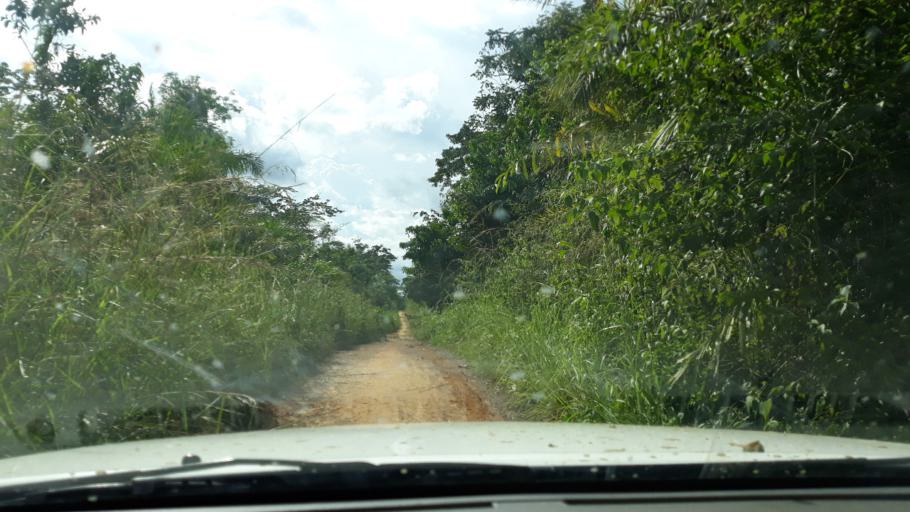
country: CD
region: Maniema
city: Kampene
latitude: -2.7560
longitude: 26.9275
